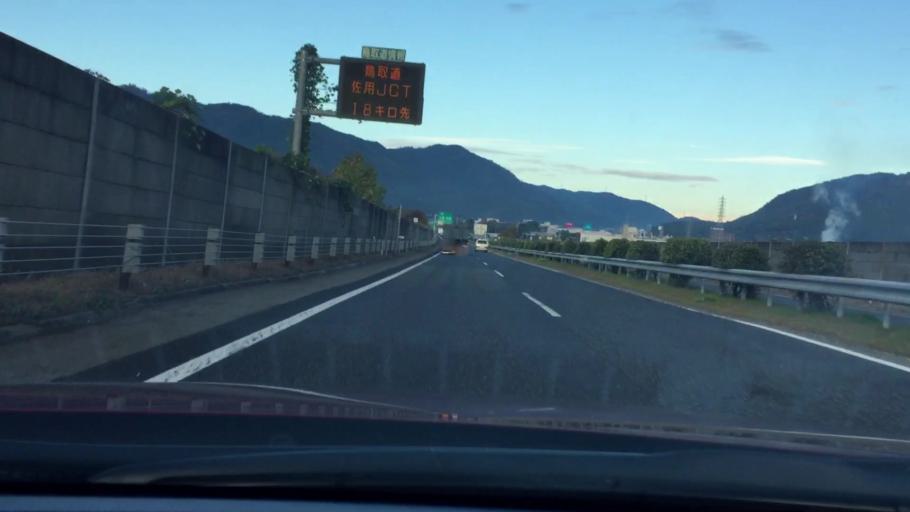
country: JP
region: Hyogo
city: Yamazakicho-nakabirose
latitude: 34.9970
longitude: 134.5581
